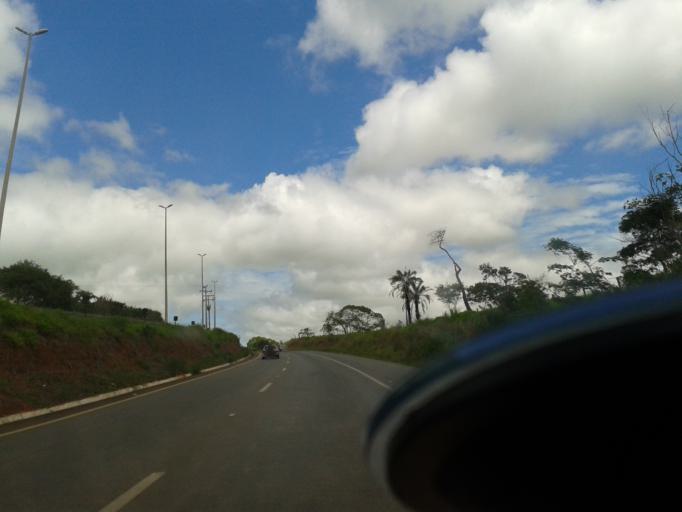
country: BR
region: Goias
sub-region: Inhumas
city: Inhumas
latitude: -16.4073
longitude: -49.4776
